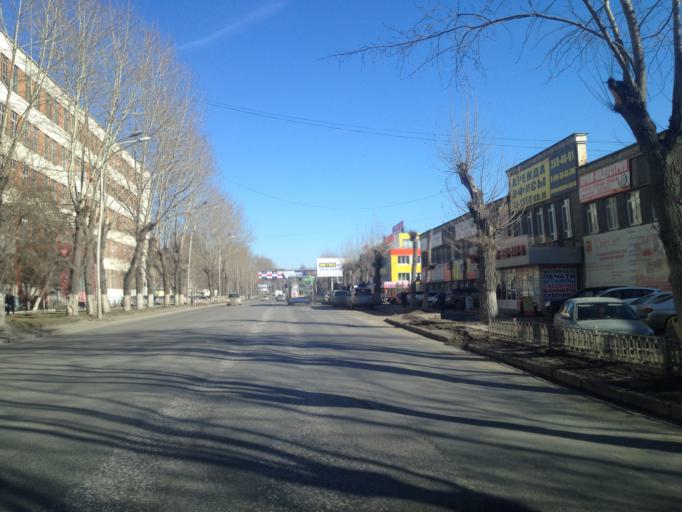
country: RU
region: Sverdlovsk
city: Yekaterinburg
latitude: 56.8247
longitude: 60.6471
